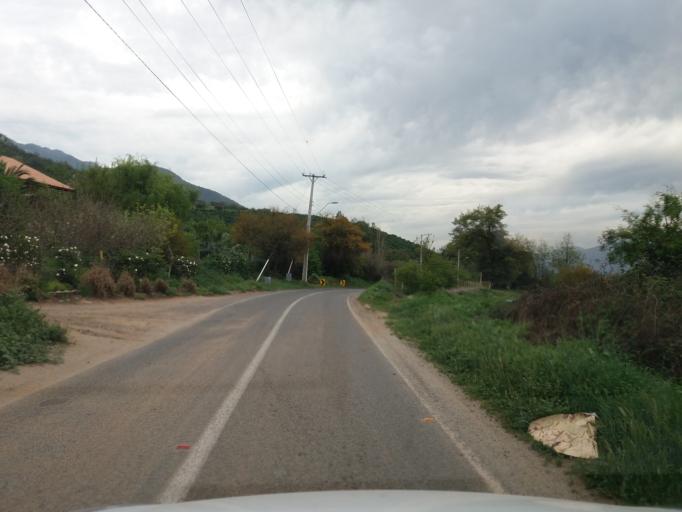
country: CL
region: Valparaiso
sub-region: Provincia de Quillota
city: Quillota
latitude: -32.9030
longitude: -71.1049
